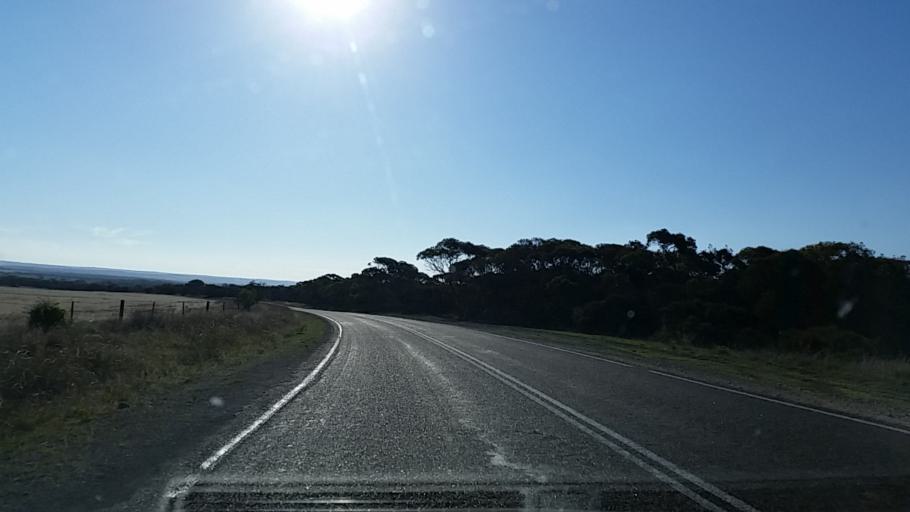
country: AU
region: South Australia
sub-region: Murray Bridge
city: Murray Bridge
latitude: -35.1276
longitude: 139.1905
